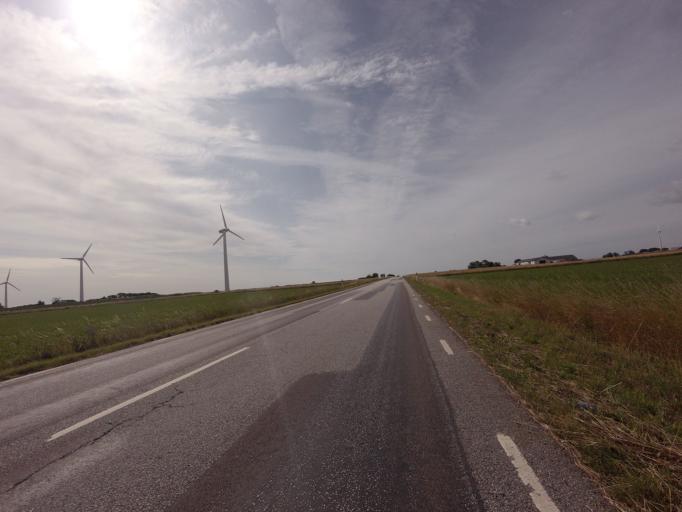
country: SE
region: Skane
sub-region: Simrishamns Kommun
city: Simrishamn
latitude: 55.5377
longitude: 14.3390
